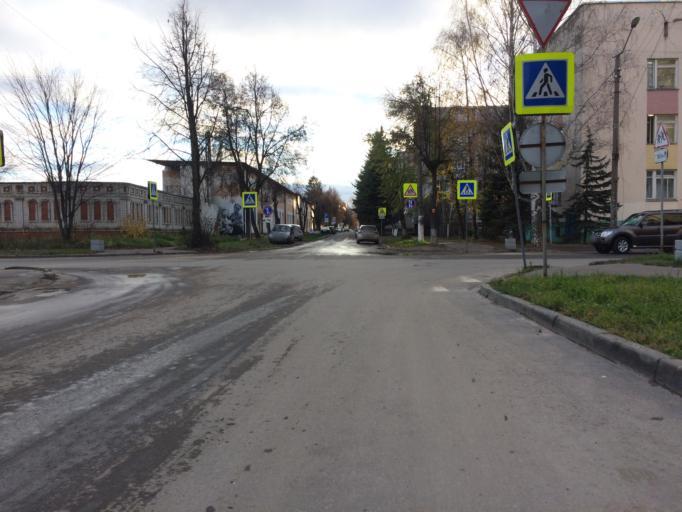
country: RU
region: Mariy-El
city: Yoshkar-Ola
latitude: 56.6423
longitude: 47.8999
